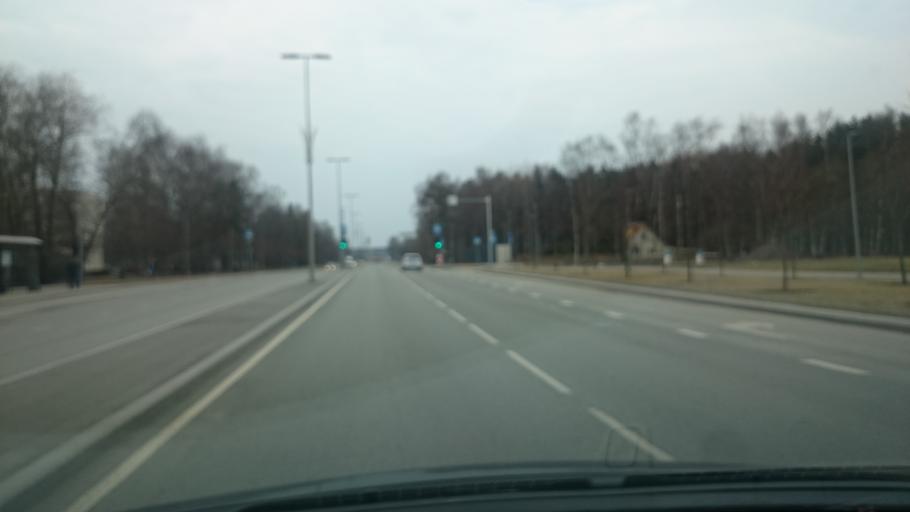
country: EE
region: Harju
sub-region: Saue vald
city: Laagri
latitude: 59.4172
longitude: 24.6550
